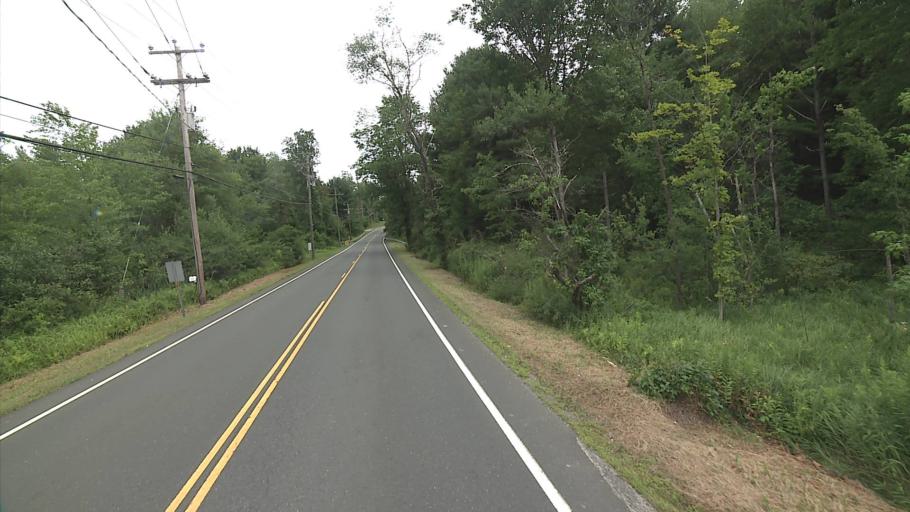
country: US
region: Connecticut
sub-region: Litchfield County
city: Winsted
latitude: 41.9629
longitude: -73.0493
